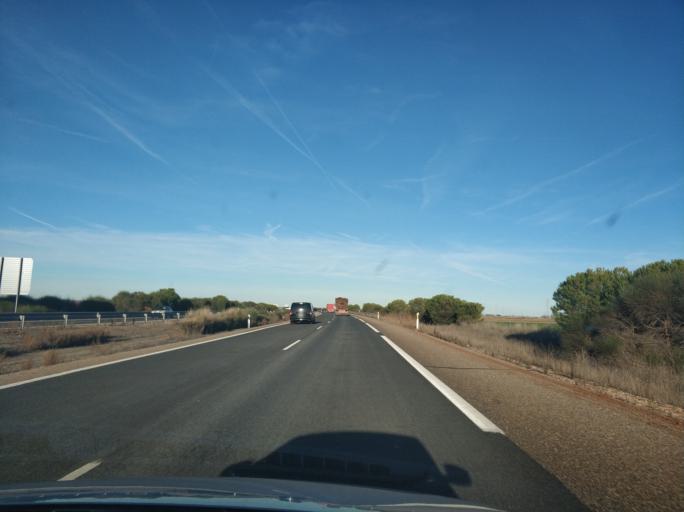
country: ES
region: Castille and Leon
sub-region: Provincia de Salamanca
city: Castellanos de Moriscos
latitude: 41.0347
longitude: -5.5654
